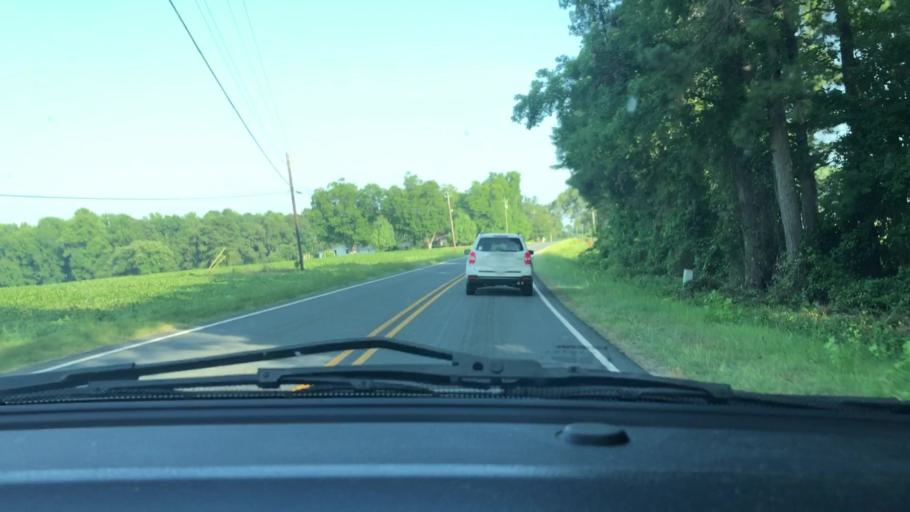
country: US
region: North Carolina
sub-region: Lee County
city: Broadway
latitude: 35.3563
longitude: -79.0788
